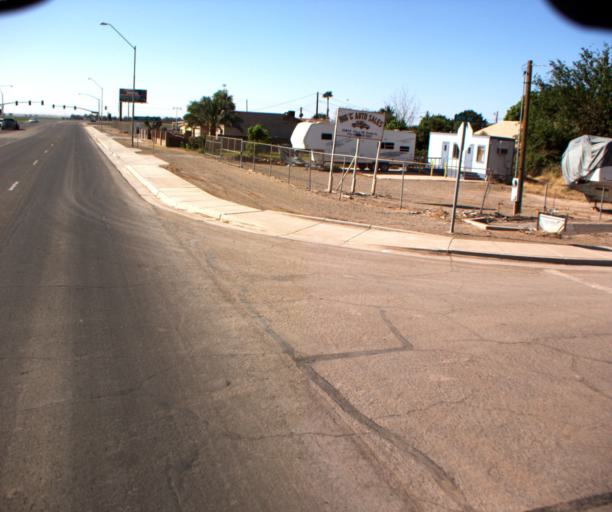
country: US
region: Arizona
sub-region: Yuma County
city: San Luis
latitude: 32.5545
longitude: -114.7849
